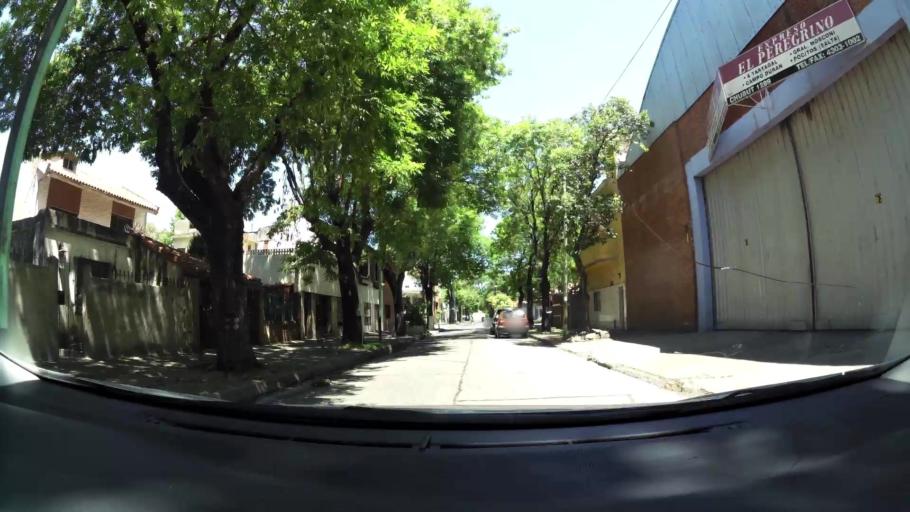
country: AR
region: Buenos Aires
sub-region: Partido de Avellaneda
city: Avellaneda
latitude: -34.6493
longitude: -58.3916
